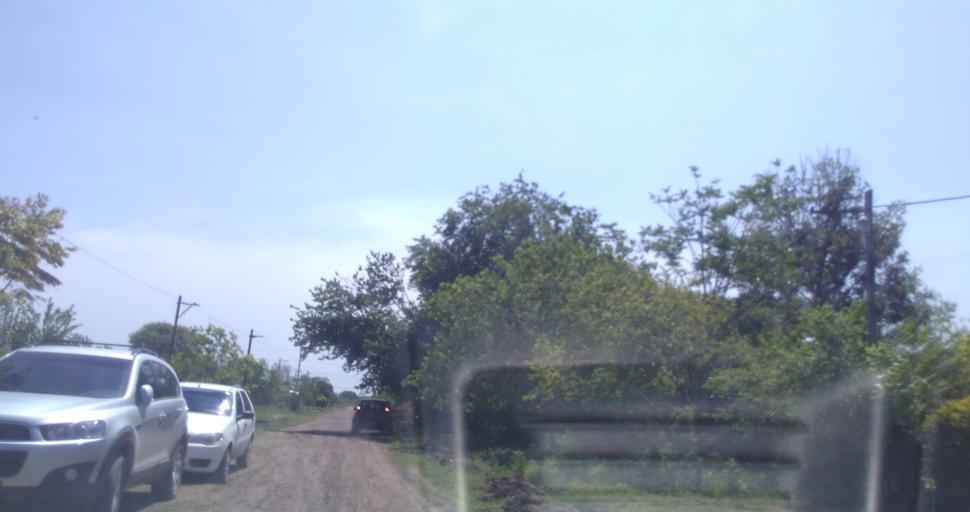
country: AR
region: Chaco
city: Fontana
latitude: -27.4042
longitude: -59.0033
